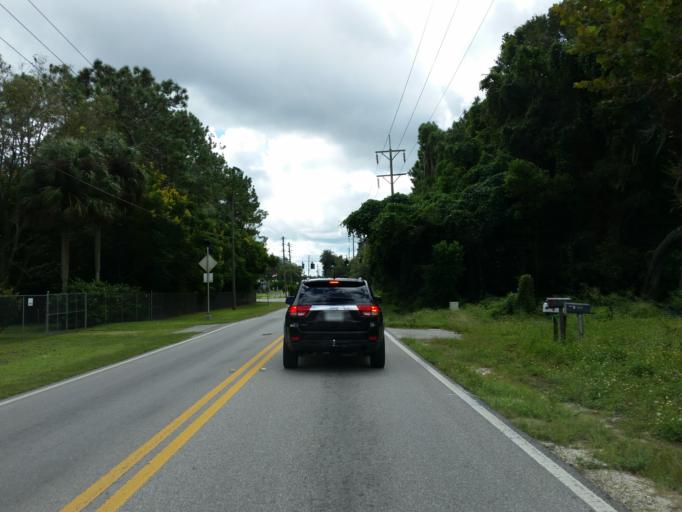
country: US
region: Florida
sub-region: Pasco County
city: Zephyrhills West
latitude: 28.2092
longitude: -82.2461
